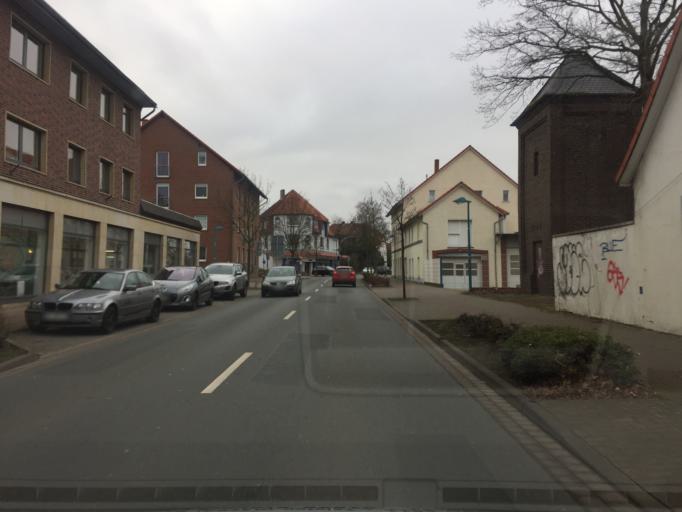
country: DE
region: Lower Saxony
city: Stadthagen
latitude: 52.3311
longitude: 9.1905
